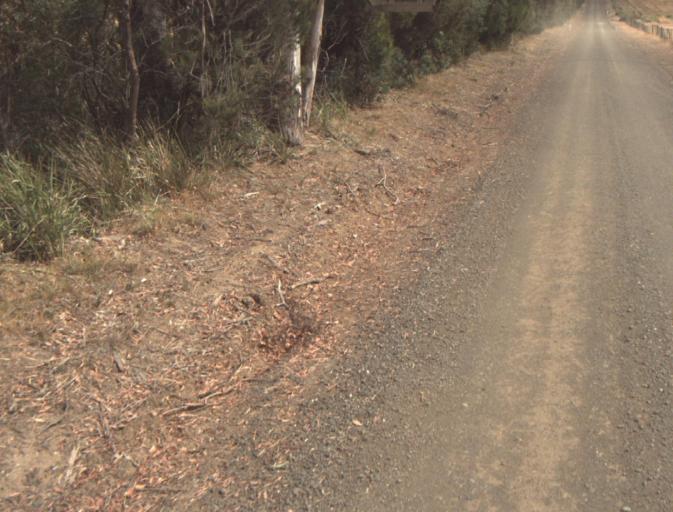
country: AU
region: Tasmania
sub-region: Launceston
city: Mayfield
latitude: -41.2772
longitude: 147.0469
